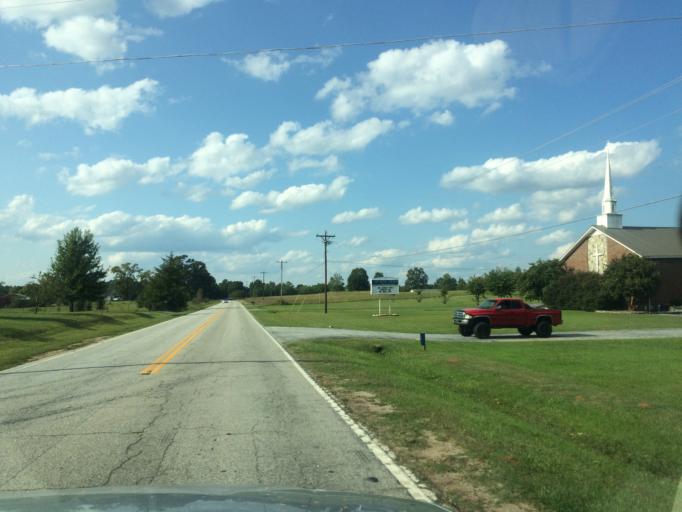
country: US
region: South Carolina
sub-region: Greenwood County
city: Ware Shoals
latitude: 34.5301
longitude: -82.1947
